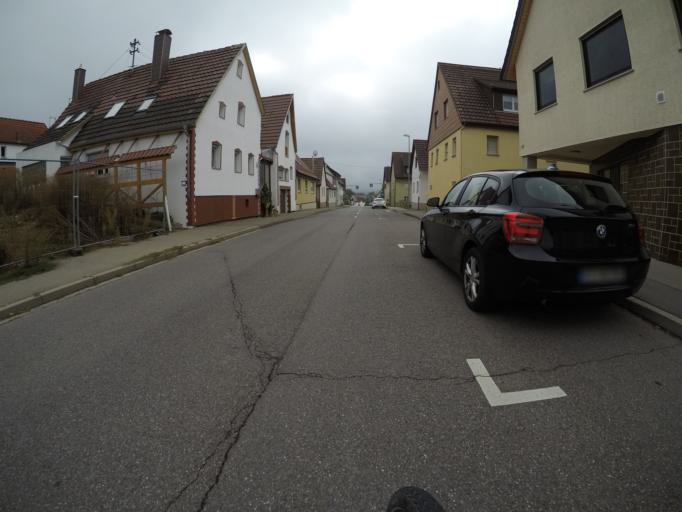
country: DE
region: Baden-Wuerttemberg
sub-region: Regierungsbezirk Stuttgart
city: Gartringen
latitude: 48.6422
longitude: 8.8935
